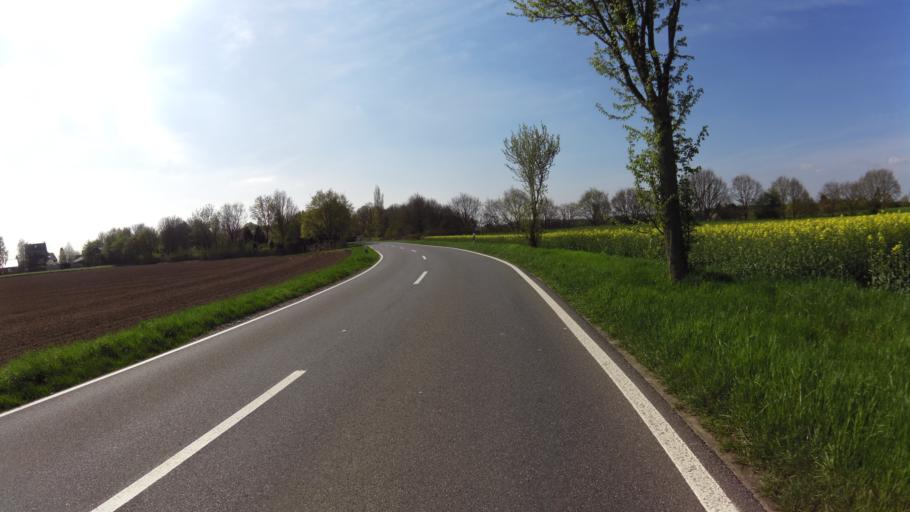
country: DE
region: North Rhine-Westphalia
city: Geilenkirchen
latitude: 50.9848
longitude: 6.0760
